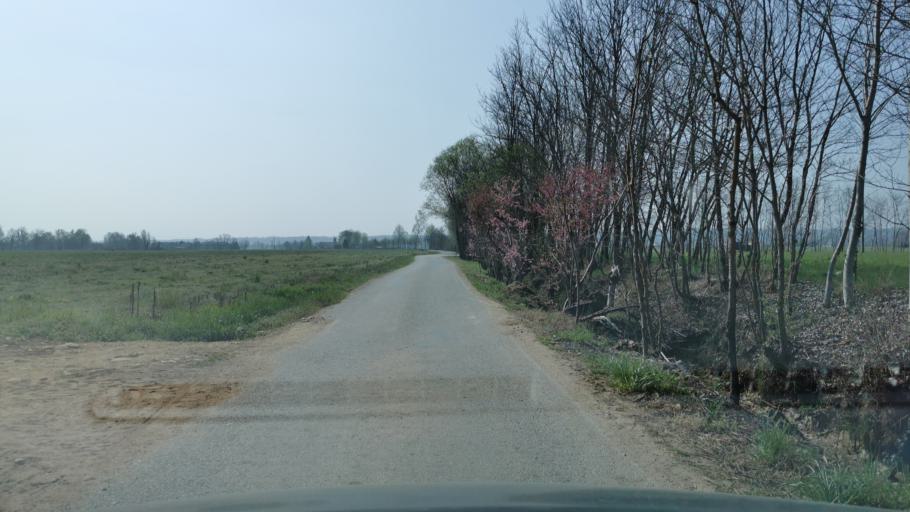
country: IT
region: Piedmont
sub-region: Provincia di Torino
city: Favria
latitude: 45.2984
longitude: 7.6948
